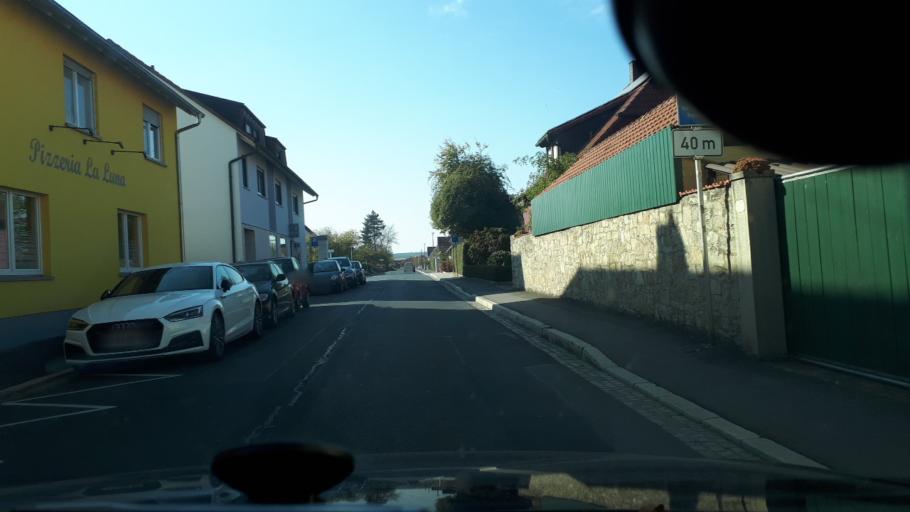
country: DE
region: Bavaria
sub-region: Regierungsbezirk Unterfranken
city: Sommerach
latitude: 49.7993
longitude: 10.2287
